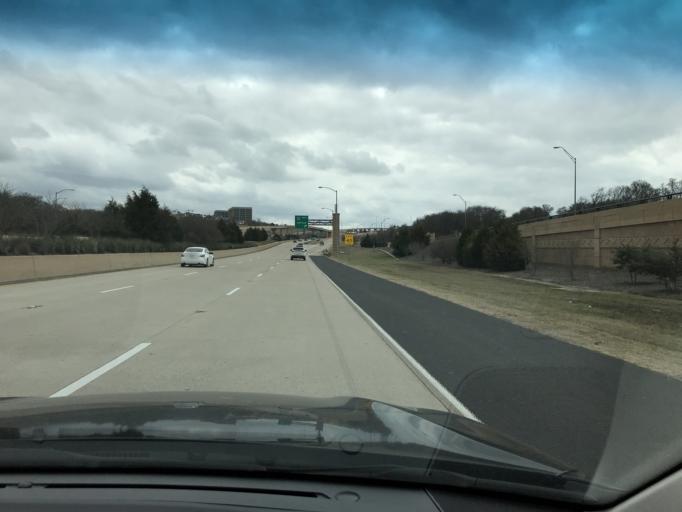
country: US
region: Texas
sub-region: Tarrant County
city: Westworth
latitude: 32.6976
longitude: -97.4057
